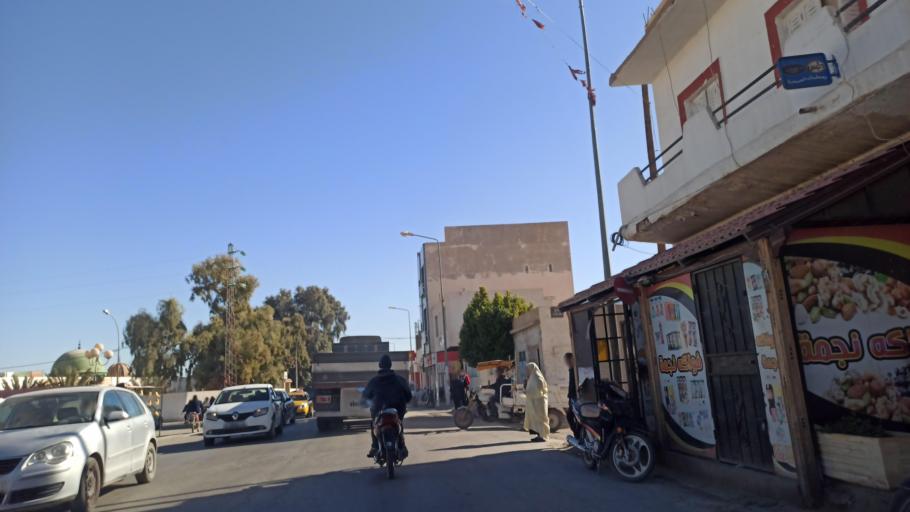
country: TN
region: Gafsa
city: Al Metlaoui
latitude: 34.3153
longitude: 8.4048
